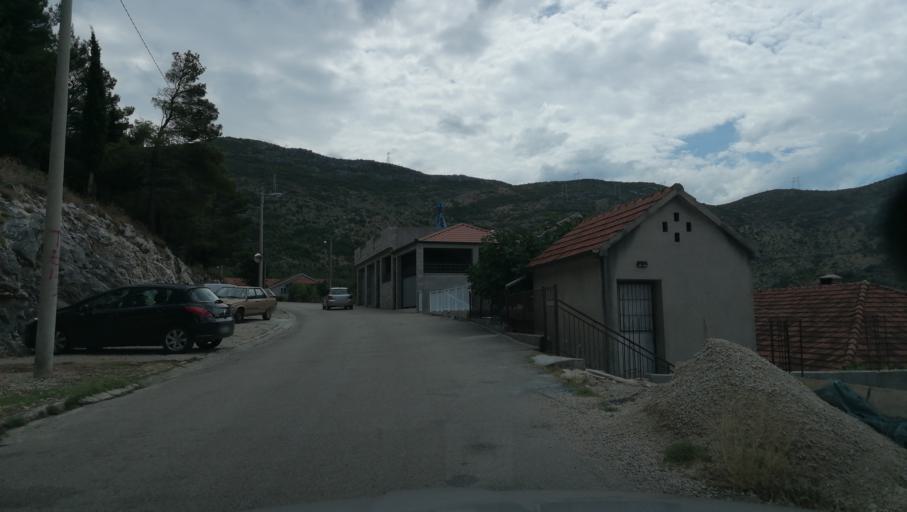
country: BA
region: Republika Srpska
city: Trebinje
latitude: 42.7089
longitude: 18.3585
